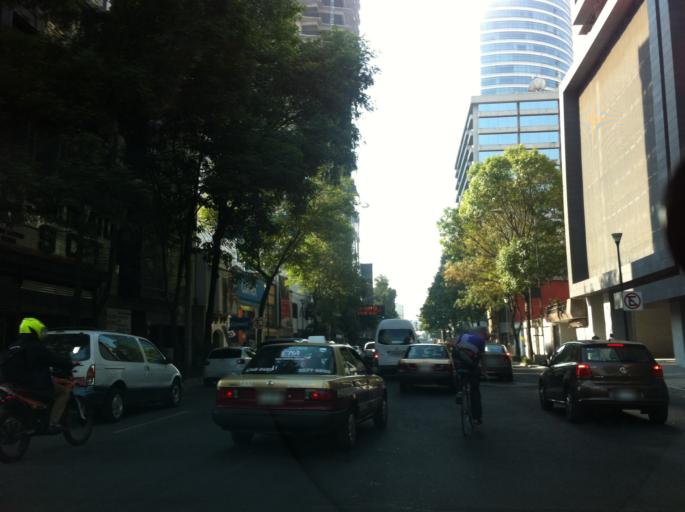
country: MX
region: Mexico City
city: Miguel Hidalgo
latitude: 19.4277
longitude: -99.1730
